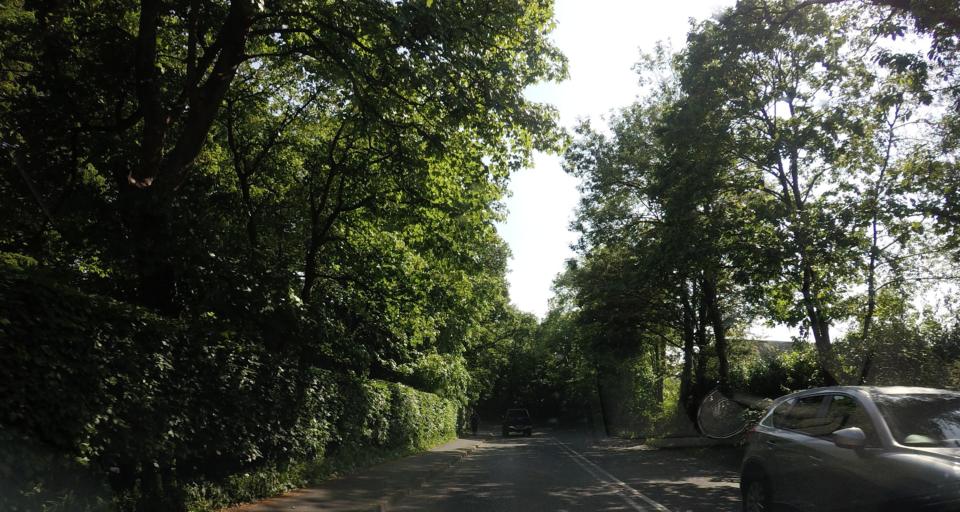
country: GB
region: England
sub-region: Cumbria
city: Cockermouth
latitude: 54.6570
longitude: -3.3714
